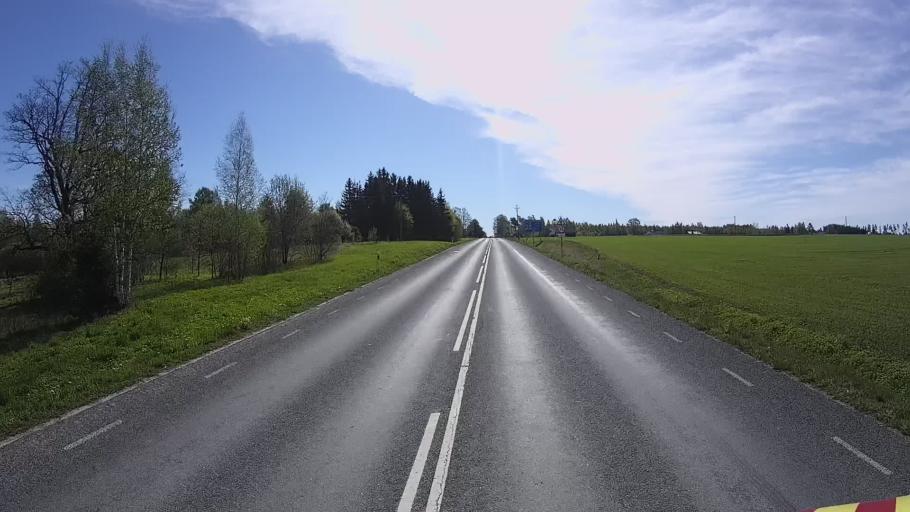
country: EE
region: Polvamaa
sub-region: Polva linn
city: Polva
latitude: 58.1565
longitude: 27.1777
